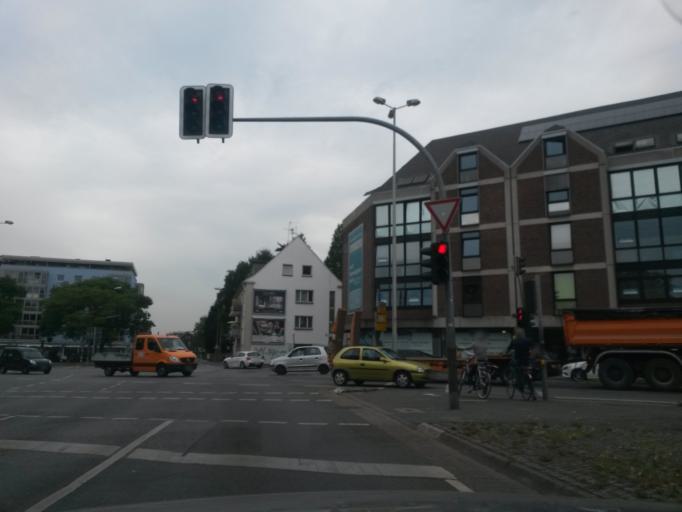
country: DE
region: North Rhine-Westphalia
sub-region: Regierungsbezirk Dusseldorf
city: Moers
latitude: 51.4531
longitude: 6.6221
